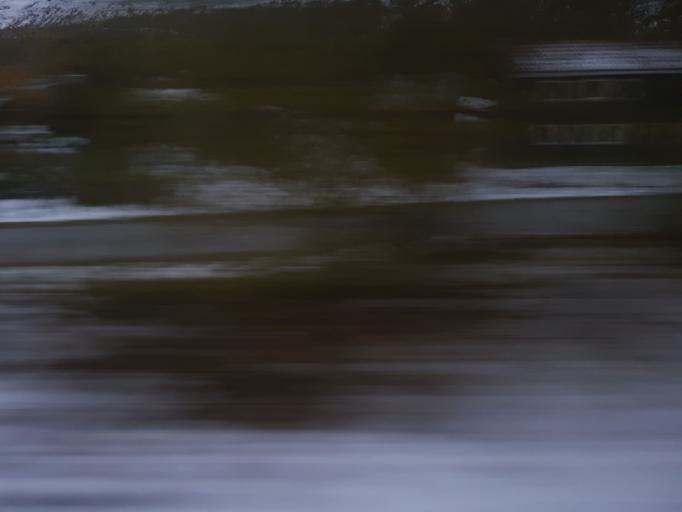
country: NO
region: Sor-Trondelag
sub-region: Oppdal
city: Oppdal
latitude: 62.5284
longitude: 9.6137
